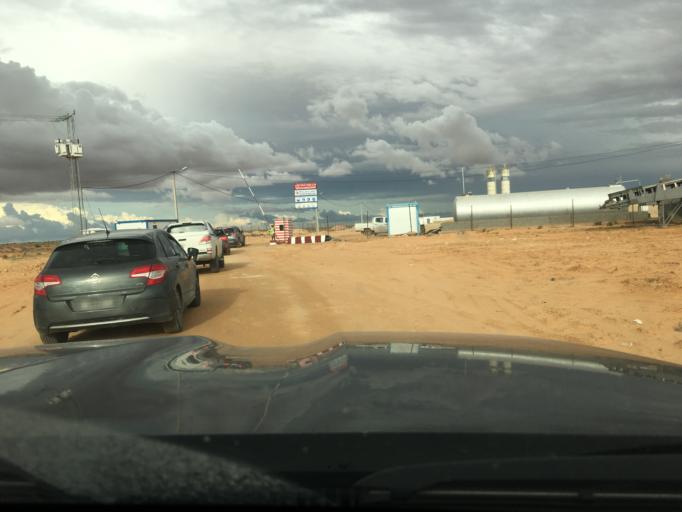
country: TN
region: Madanin
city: Medenine
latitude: 33.2668
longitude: 10.5698
